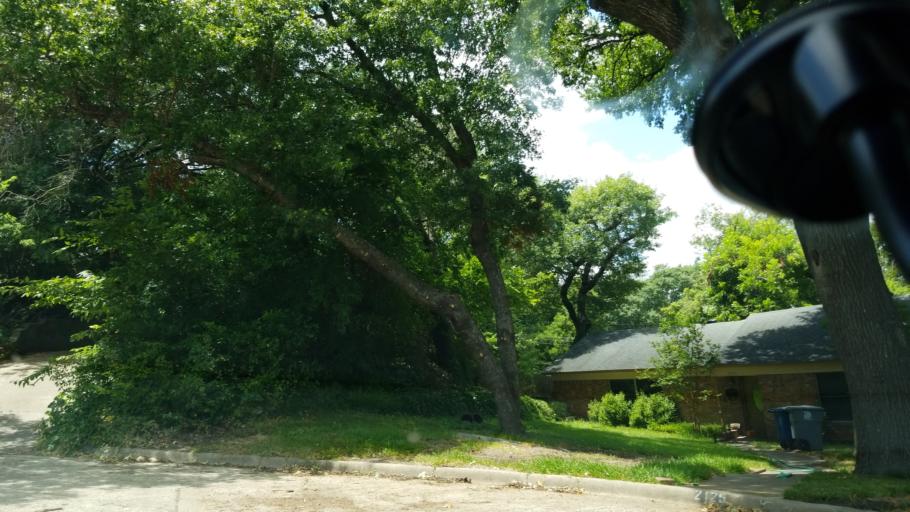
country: US
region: Texas
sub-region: Dallas County
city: Cockrell Hill
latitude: 32.7004
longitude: -96.8534
